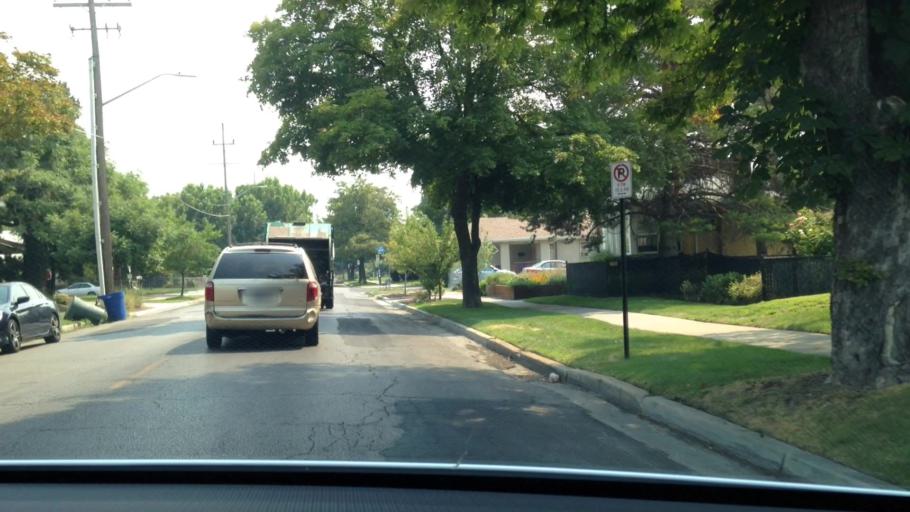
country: US
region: Utah
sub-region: Salt Lake County
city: South Salt Lake
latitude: 40.7279
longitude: -111.8769
